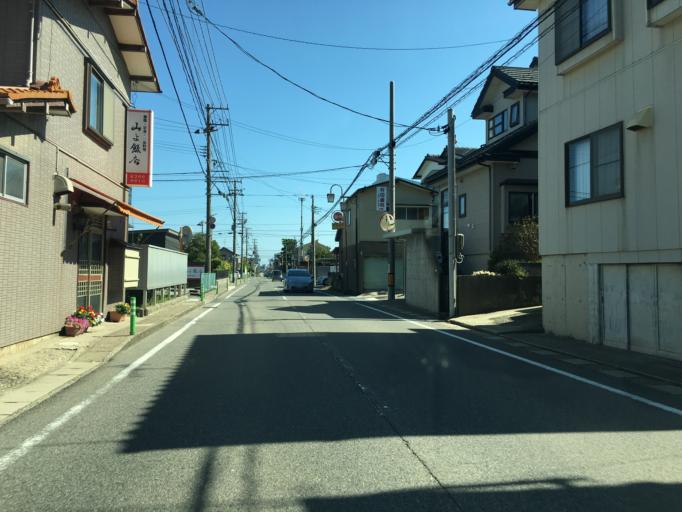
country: JP
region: Niigata
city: Niigata-shi
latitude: 37.8999
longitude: 138.9966
